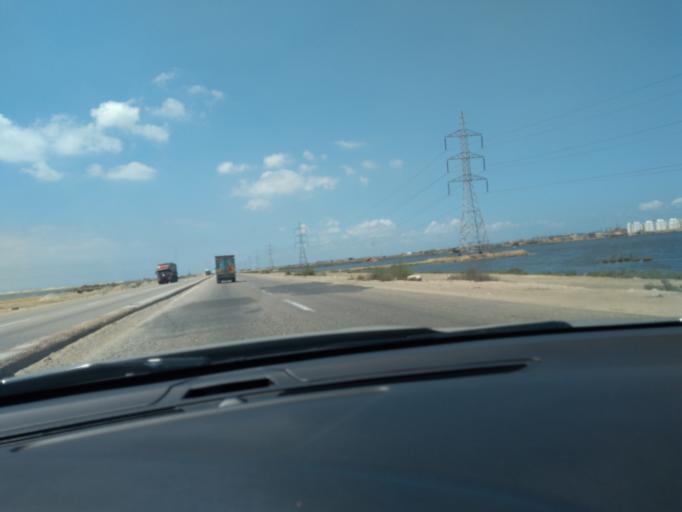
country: EG
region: Muhafazat Bur Sa`id
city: Port Said
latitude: 31.3007
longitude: 32.1496
